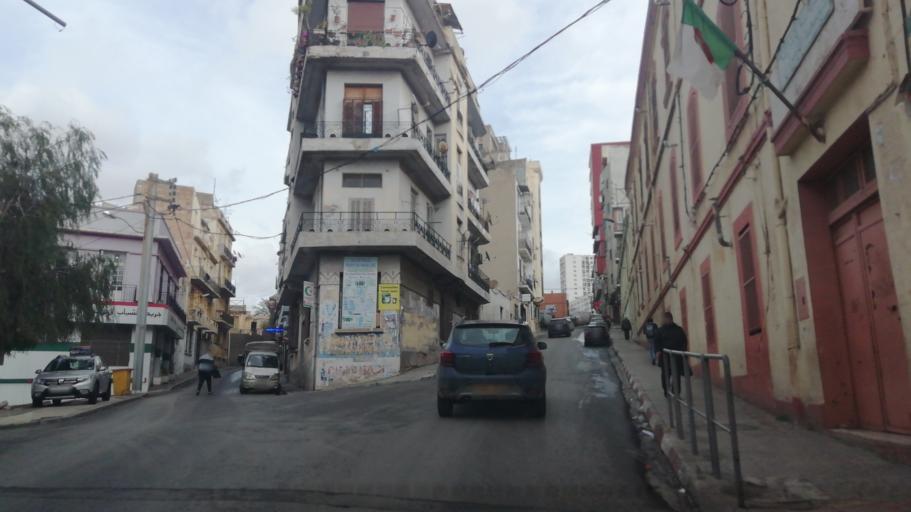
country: DZ
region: Oran
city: Oran
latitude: 35.7025
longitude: -0.6334
